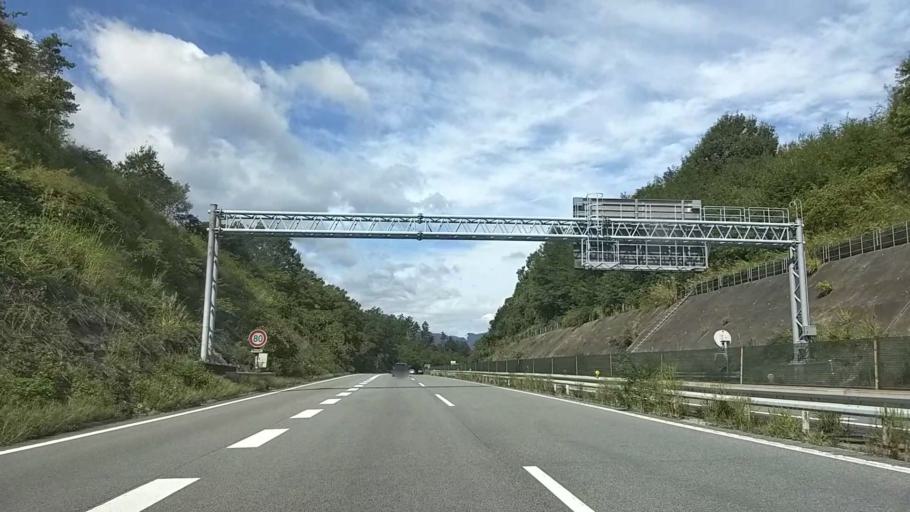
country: JP
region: Yamanashi
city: Nirasaki
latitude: 35.7921
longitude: 138.4055
